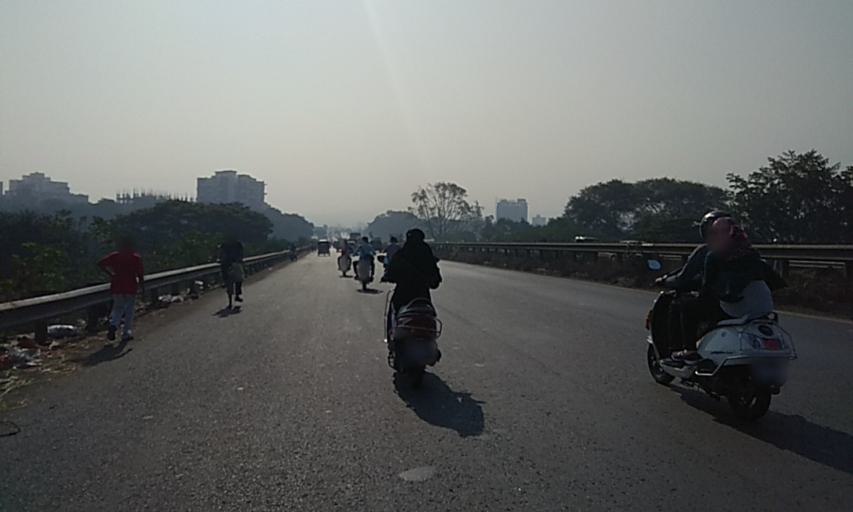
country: IN
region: Maharashtra
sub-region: Pune Division
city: Kharakvasla
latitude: 18.4763
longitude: 73.8080
